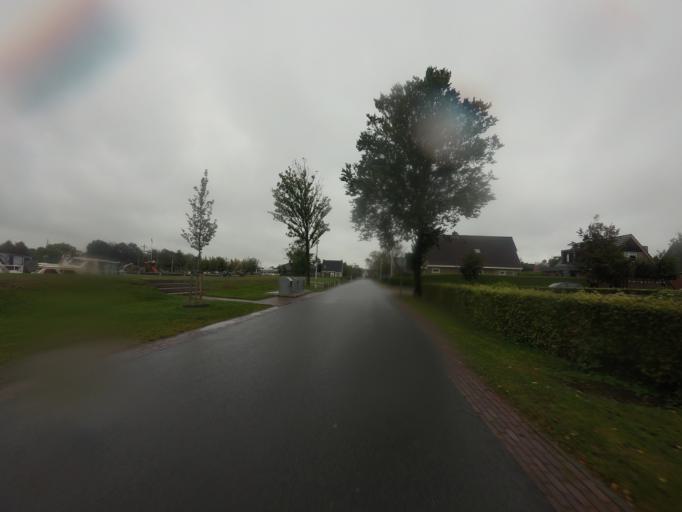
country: NL
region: Friesland
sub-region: Gemeente Tytsjerksteradiel
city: Garyp
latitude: 53.1307
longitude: 5.9403
